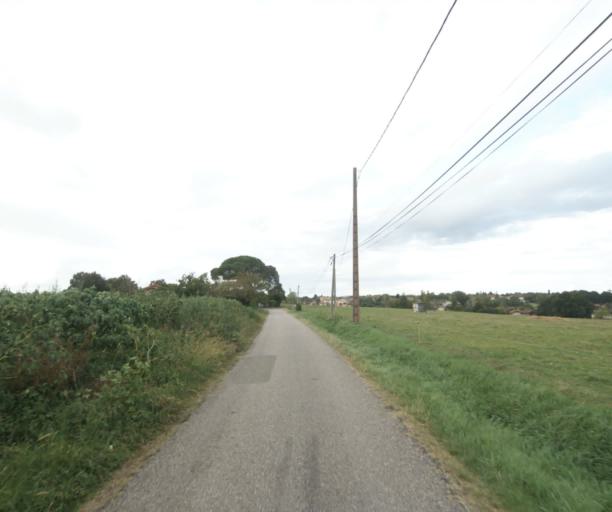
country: FR
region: Midi-Pyrenees
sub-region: Departement du Gers
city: Eauze
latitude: 43.9421
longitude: 0.0820
